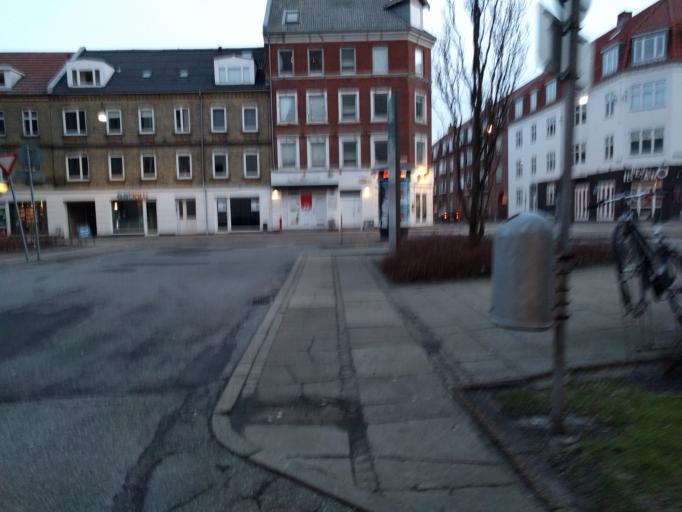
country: DK
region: North Denmark
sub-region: Alborg Kommune
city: Aalborg
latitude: 57.0492
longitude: 9.9116
